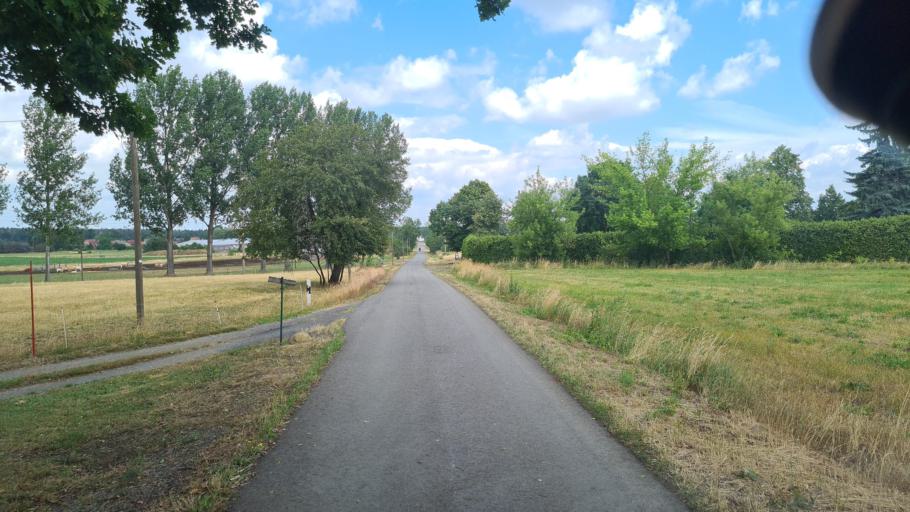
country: DE
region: Brandenburg
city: Calau
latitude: 51.7543
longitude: 13.9077
